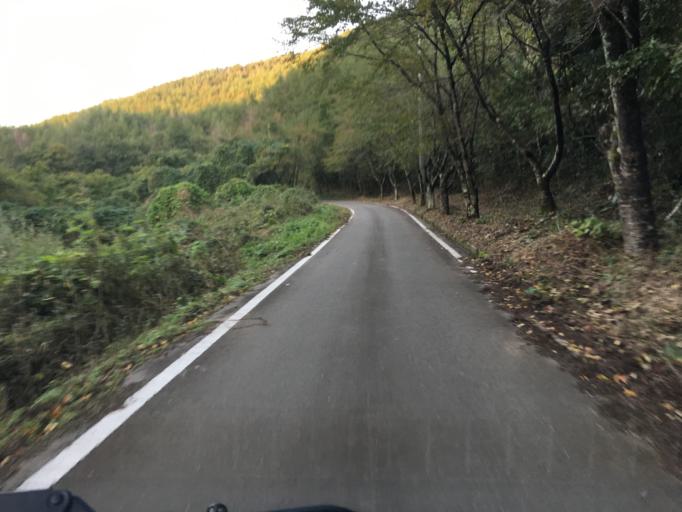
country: JP
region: Fukushima
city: Yanagawamachi-saiwaicho
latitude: 37.8467
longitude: 140.6320
